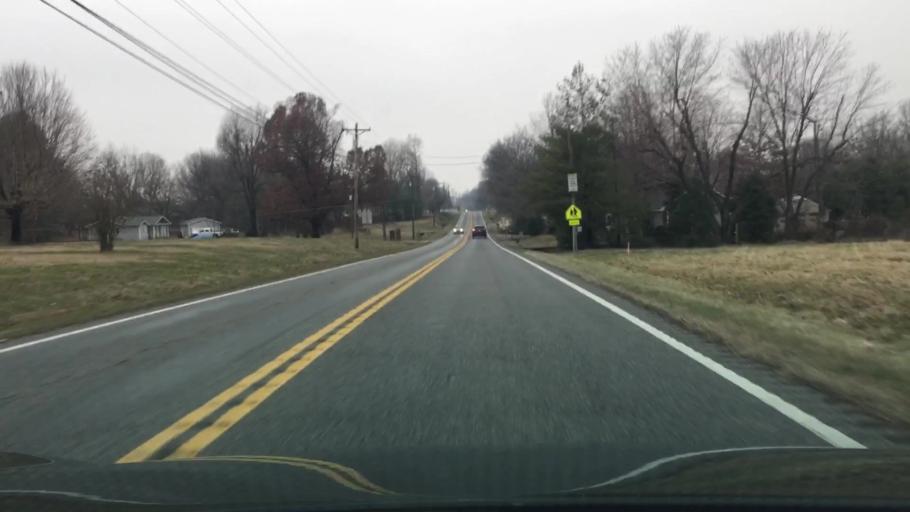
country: US
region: Kentucky
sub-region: Livingston County
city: Ledbetter
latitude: 36.9714
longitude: -88.4640
